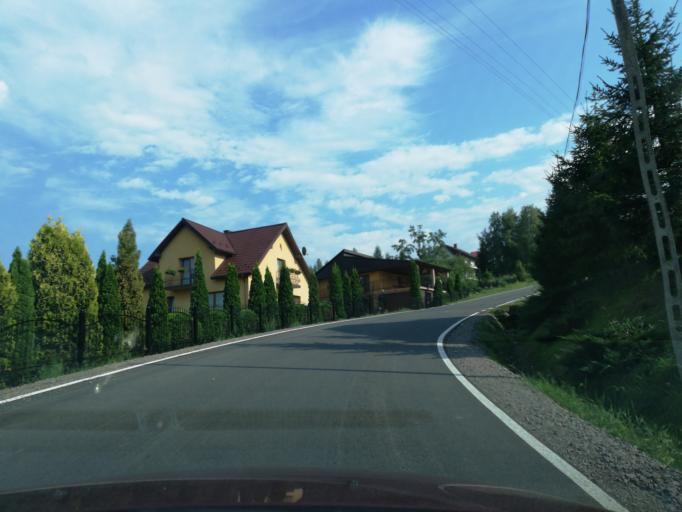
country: PL
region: Lesser Poland Voivodeship
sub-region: Powiat nowosadecki
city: Nawojowa
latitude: 49.5382
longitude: 20.7410
